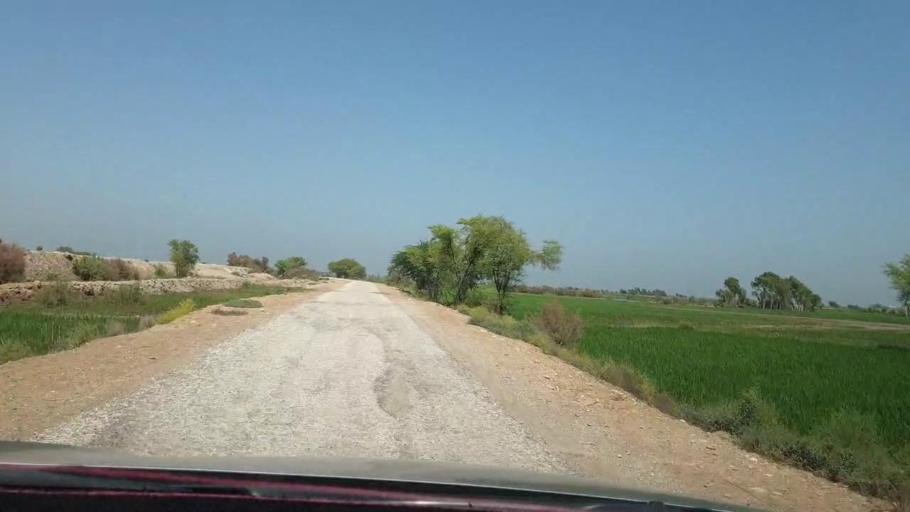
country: PK
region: Sindh
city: Warah
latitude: 27.5508
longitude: 67.7376
